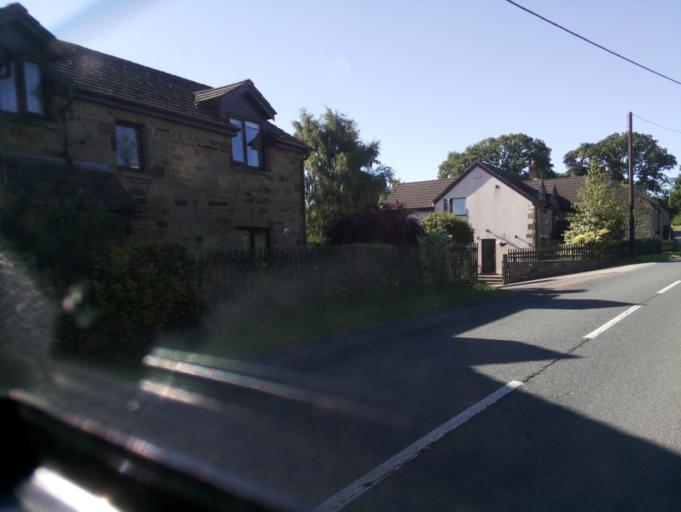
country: GB
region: England
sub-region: Gloucestershire
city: Coleford
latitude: 51.8157
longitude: -2.6229
